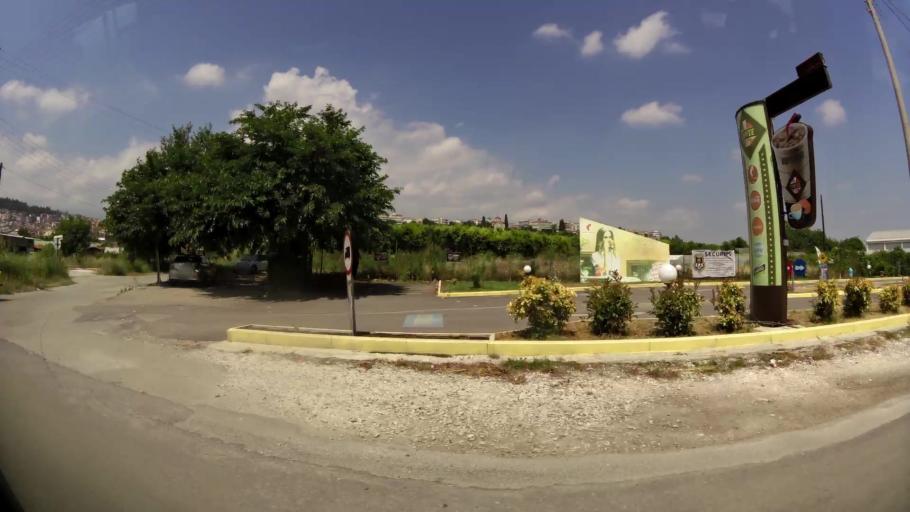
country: GR
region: Central Macedonia
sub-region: Nomos Imathias
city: Veroia
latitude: 40.5236
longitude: 22.2146
